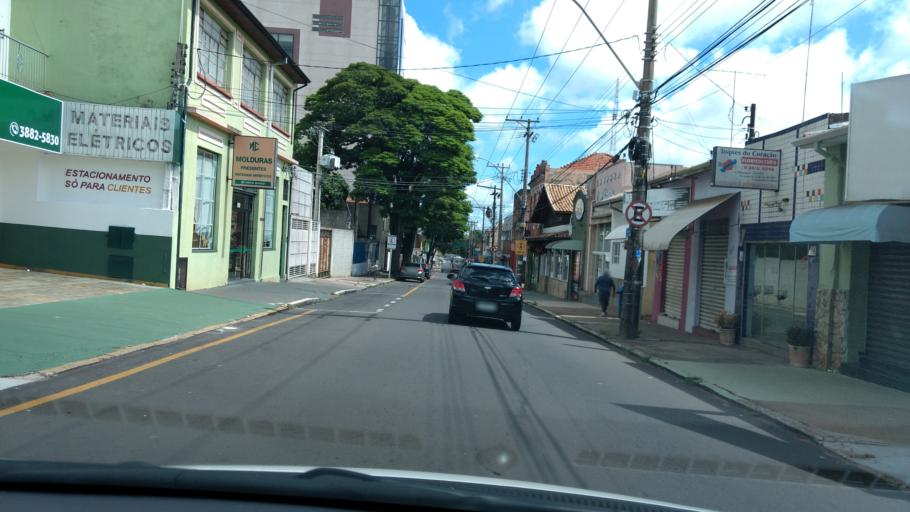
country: BR
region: Sao Paulo
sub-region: Botucatu
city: Botucatu
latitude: -22.8867
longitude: -48.4399
